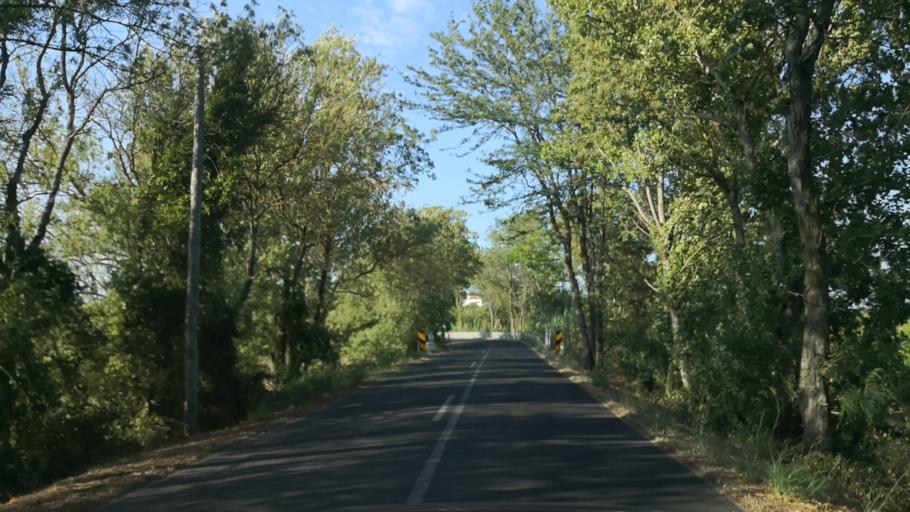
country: PT
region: Santarem
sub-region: Santarem
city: Santarem
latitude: 39.2680
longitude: -8.6629
